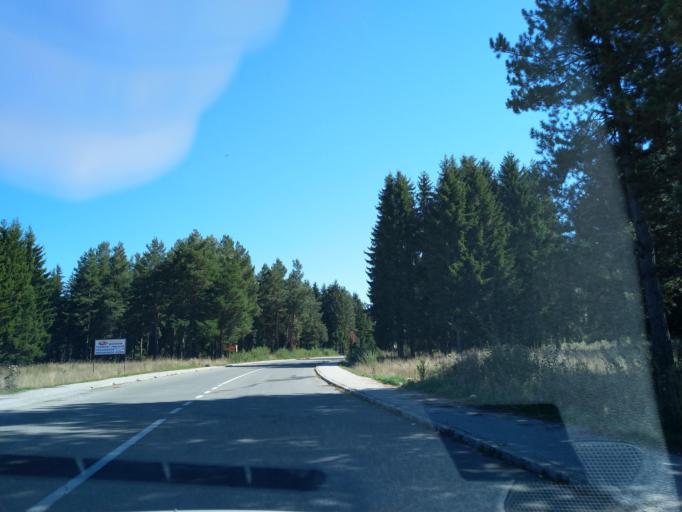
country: RS
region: Central Serbia
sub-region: Zlatiborski Okrug
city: Sjenica
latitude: 43.2724
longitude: 20.0166
